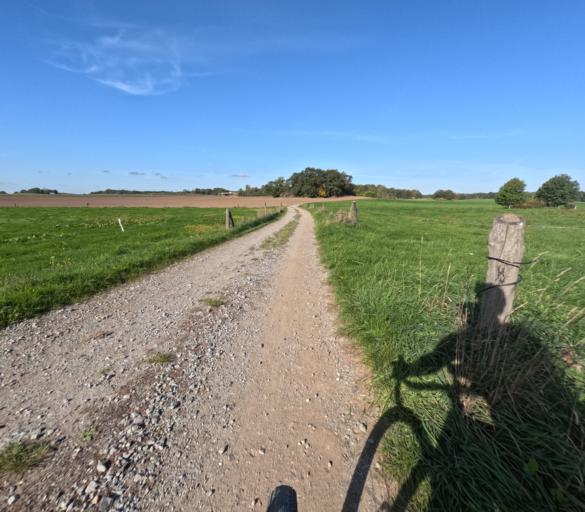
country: DE
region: Saxony
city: Radeburg
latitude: 51.1702
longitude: 13.7561
